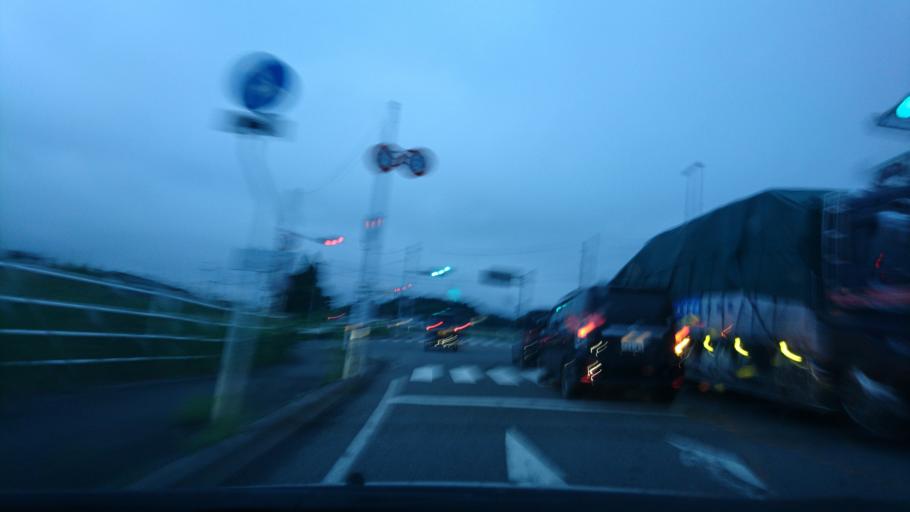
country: JP
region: Iwate
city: Ichinoseki
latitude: 38.7999
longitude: 141.0559
